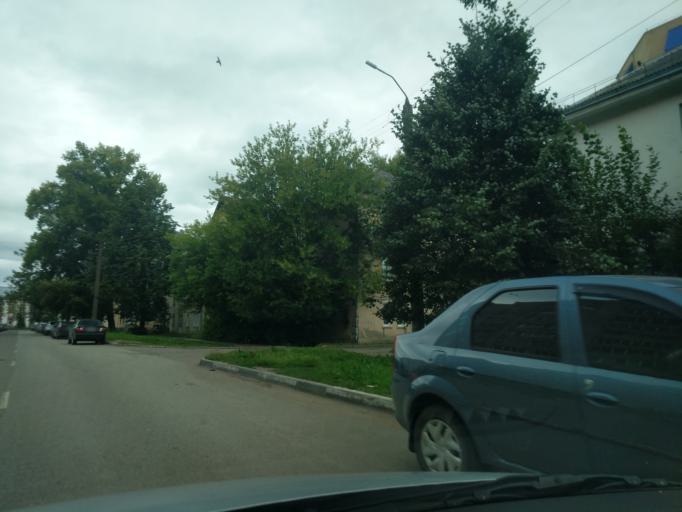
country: RU
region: Kirov
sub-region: Kirovo-Chepetskiy Rayon
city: Kirov
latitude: 58.6364
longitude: 49.6173
